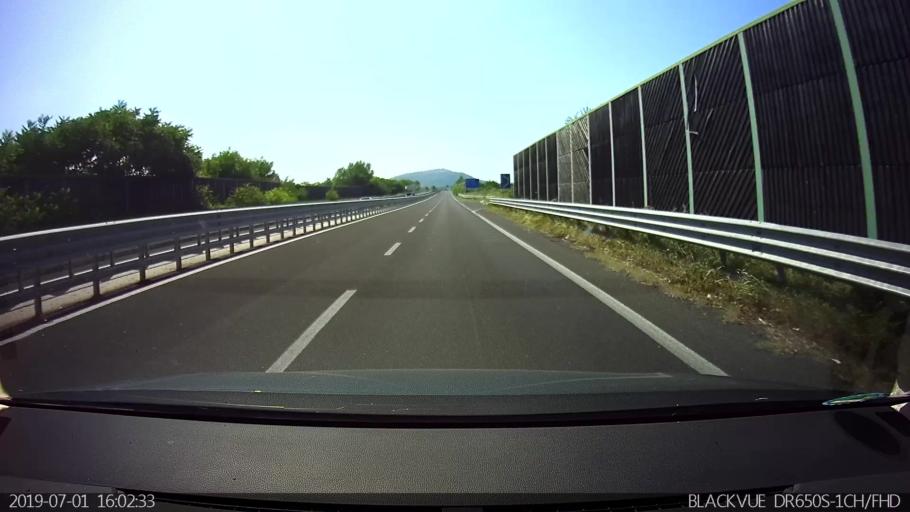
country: IT
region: Latium
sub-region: Provincia di Frosinone
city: Tecchiena
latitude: 41.6710
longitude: 13.3541
